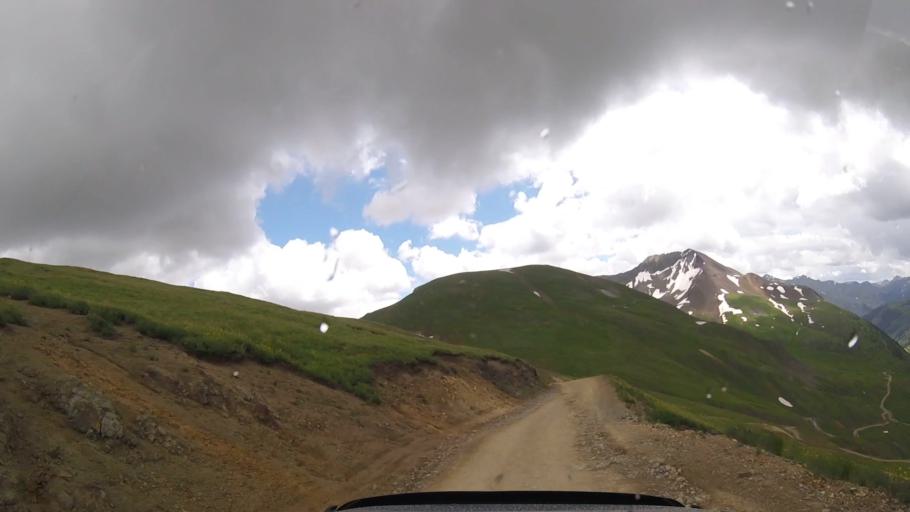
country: US
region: Colorado
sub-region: Ouray County
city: Ouray
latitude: 37.9649
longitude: -107.5771
